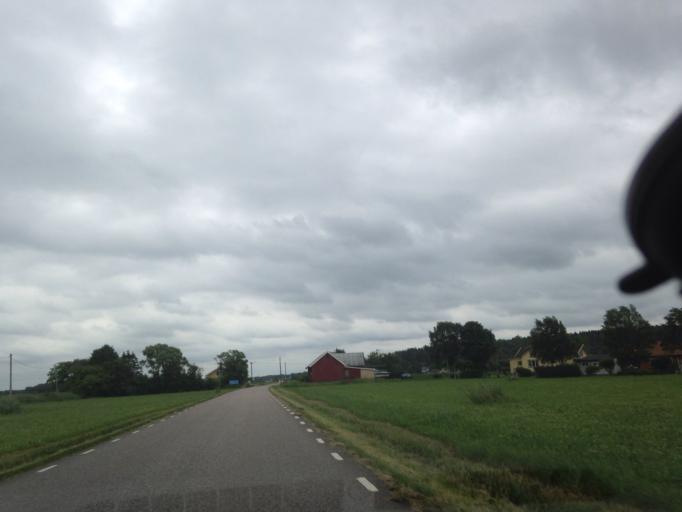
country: SE
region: Vaestra Goetaland
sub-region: Kungalvs Kommun
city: Kode
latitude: 57.8329
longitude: 11.8030
